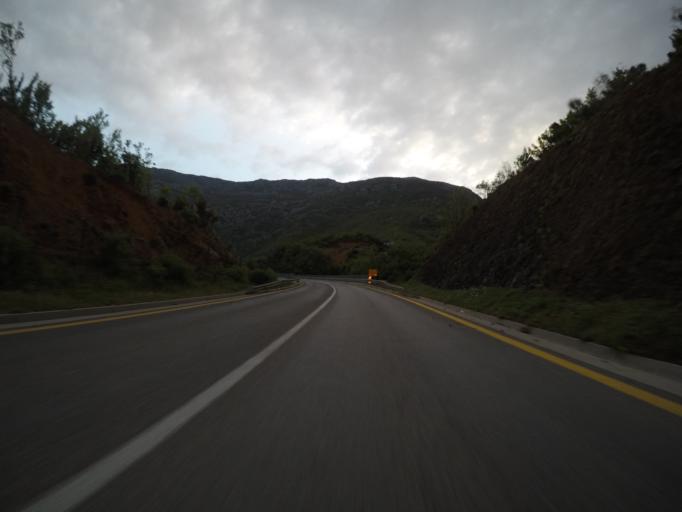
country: ME
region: Bar
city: Sutomore
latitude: 42.1611
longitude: 19.0251
